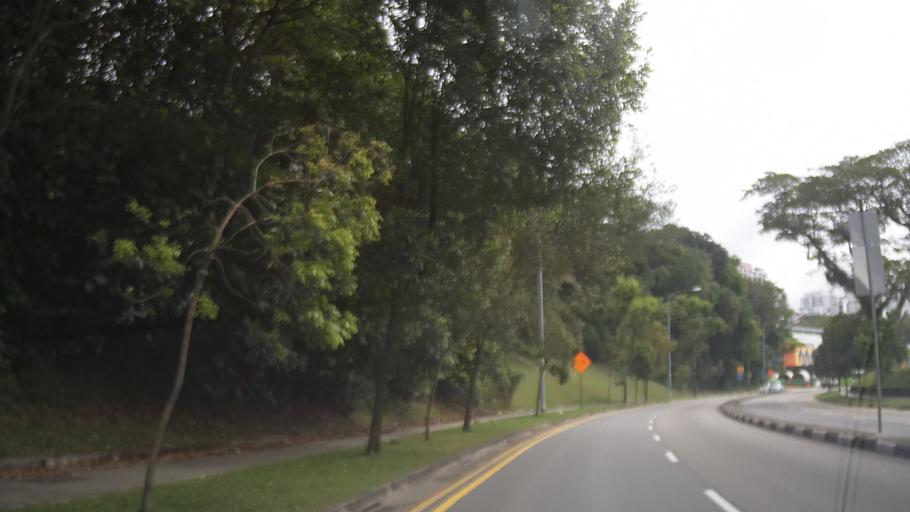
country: MY
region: Johor
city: Johor Bahru
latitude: 1.4379
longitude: 103.7724
